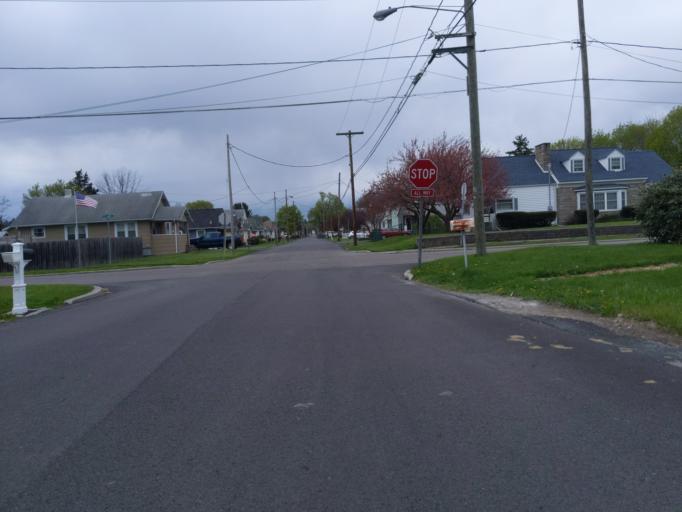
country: US
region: New York
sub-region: Chemung County
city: Southport
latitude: 42.0627
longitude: -76.8121
